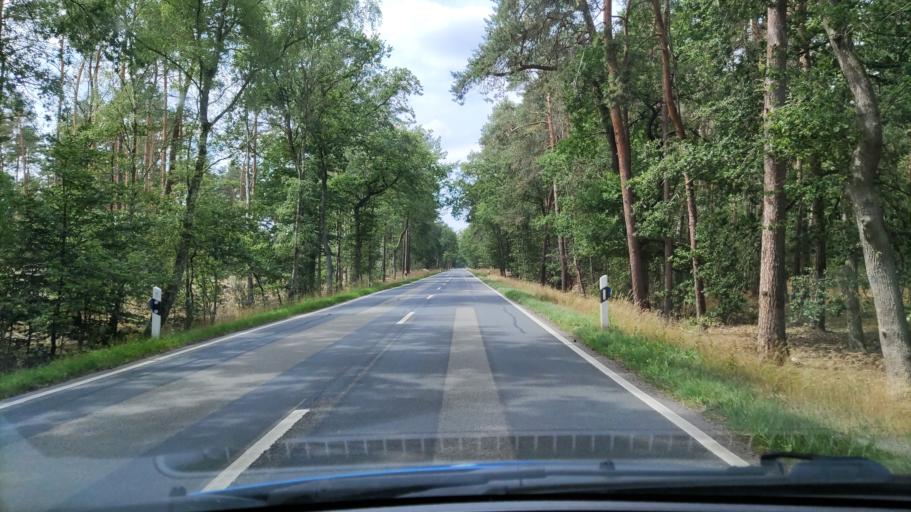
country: DE
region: Lower Saxony
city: Bergen an der Dumme
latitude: 52.9093
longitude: 10.9377
